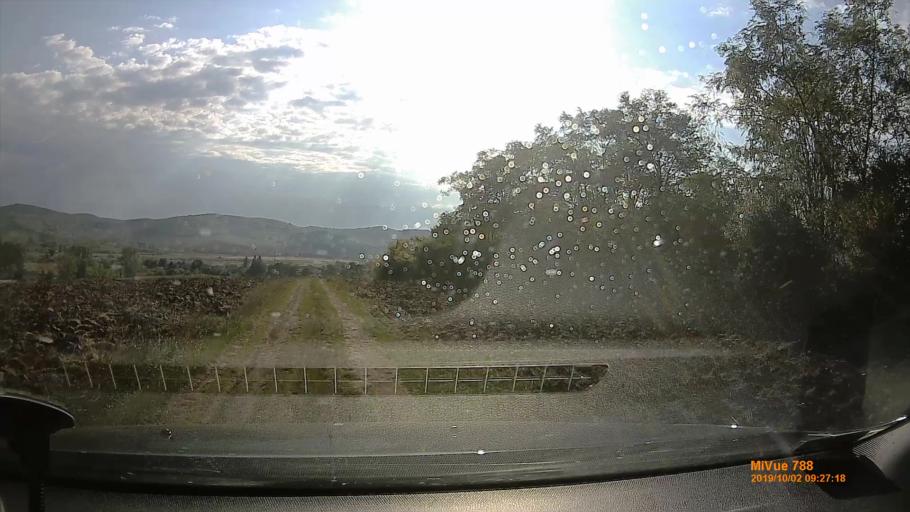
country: HU
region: Nograd
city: Kazar
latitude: 48.0222
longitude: 19.8172
